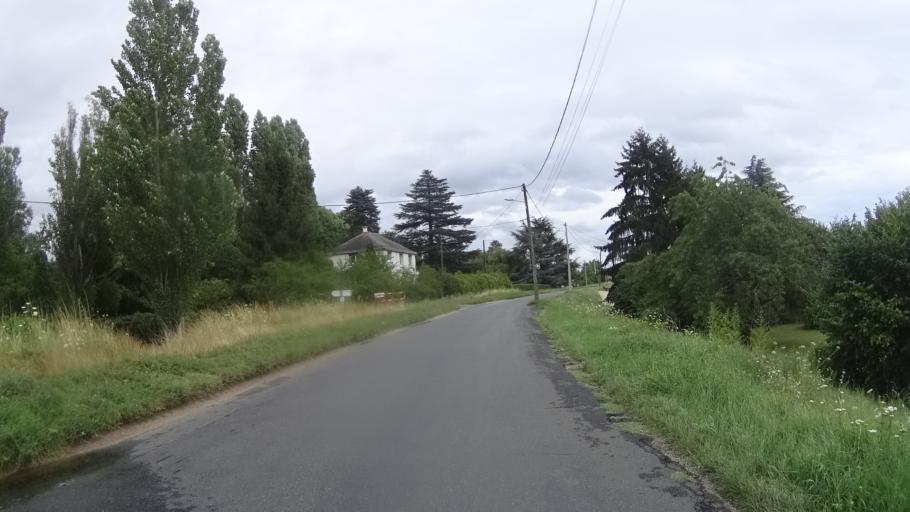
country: FR
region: Centre
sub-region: Departement du Loiret
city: Jargeau
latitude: 47.8684
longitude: 2.1159
